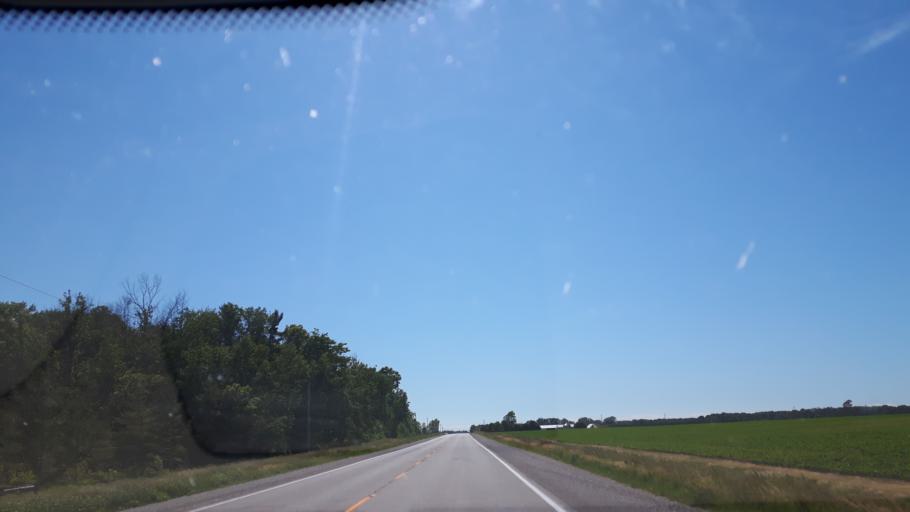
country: CA
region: Ontario
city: Bluewater
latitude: 43.4275
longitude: -81.5647
